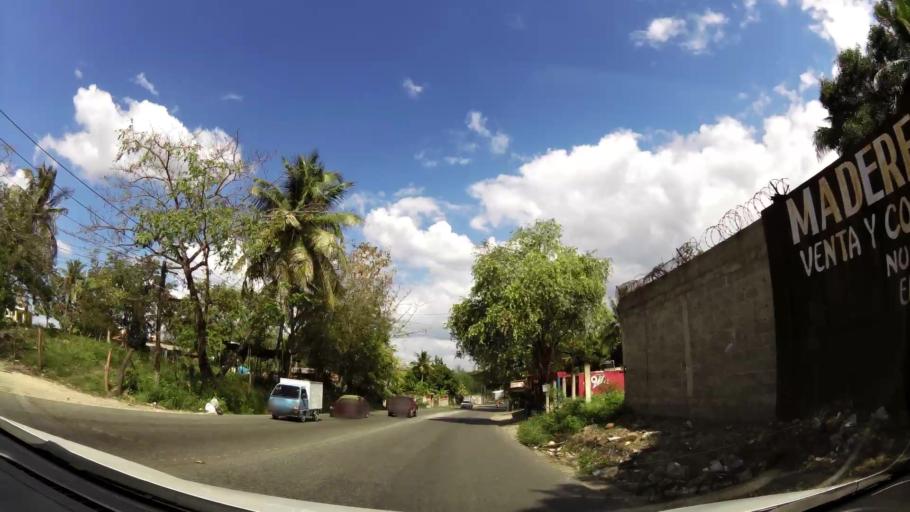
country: DO
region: San Cristobal
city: Bajos de Haina
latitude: 18.4276
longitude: -70.0613
